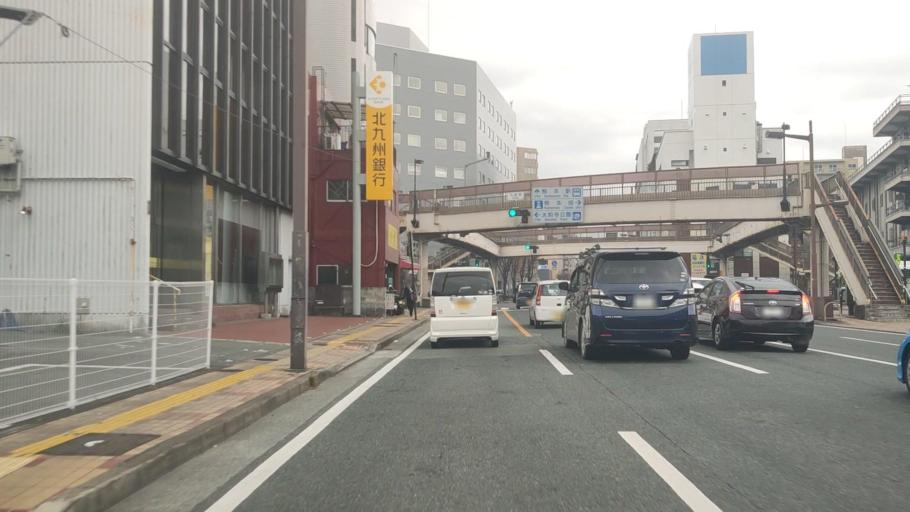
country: JP
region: Kumamoto
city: Kumamoto
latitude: 32.8002
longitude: 130.7181
